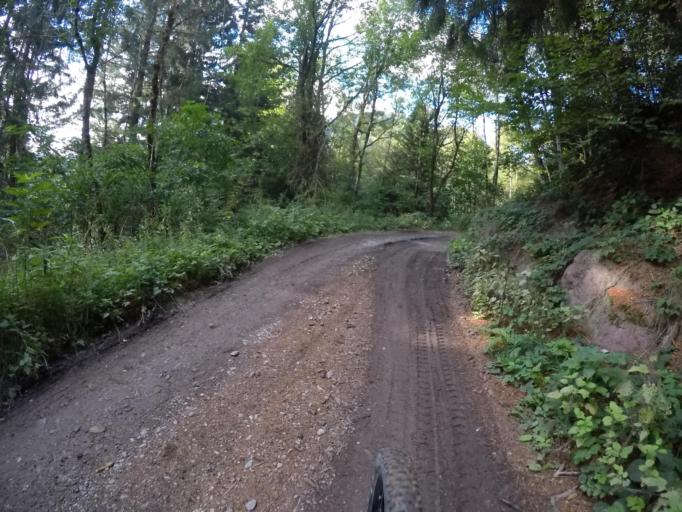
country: IT
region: Friuli Venezia Giulia
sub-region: Provincia di Udine
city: Ligosullo
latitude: 46.5387
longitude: 13.0881
